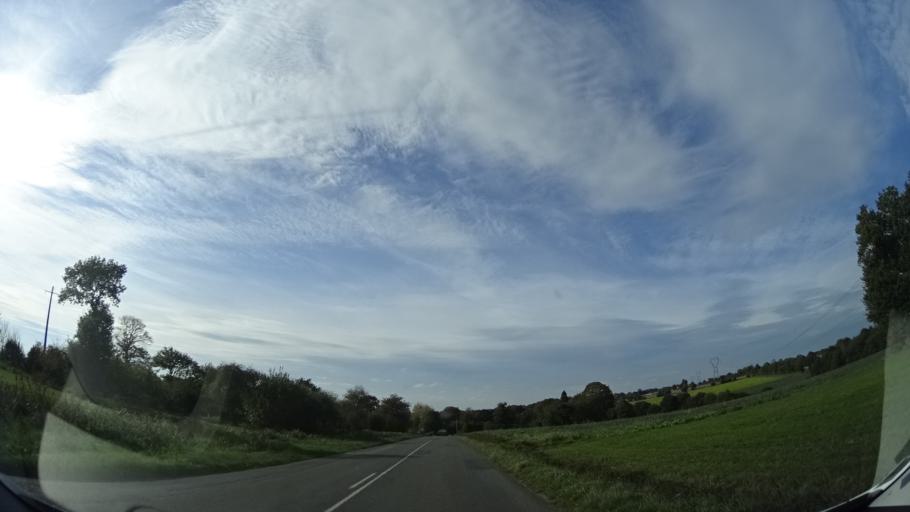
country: FR
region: Brittany
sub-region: Departement d'Ille-et-Vilaine
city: Romille
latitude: 48.2168
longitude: -1.8733
